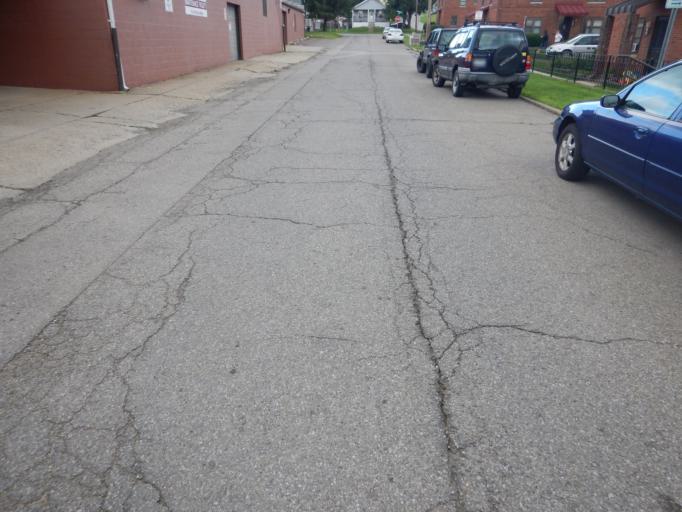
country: US
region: Ohio
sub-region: Muskingum County
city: Zanesville
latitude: 39.9271
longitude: -82.0138
